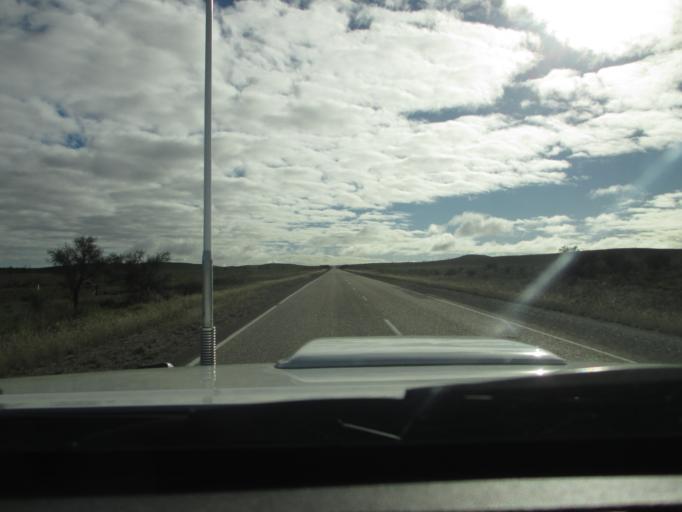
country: AU
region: South Australia
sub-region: Peterborough
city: Peterborough
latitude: -32.5785
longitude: 138.5620
